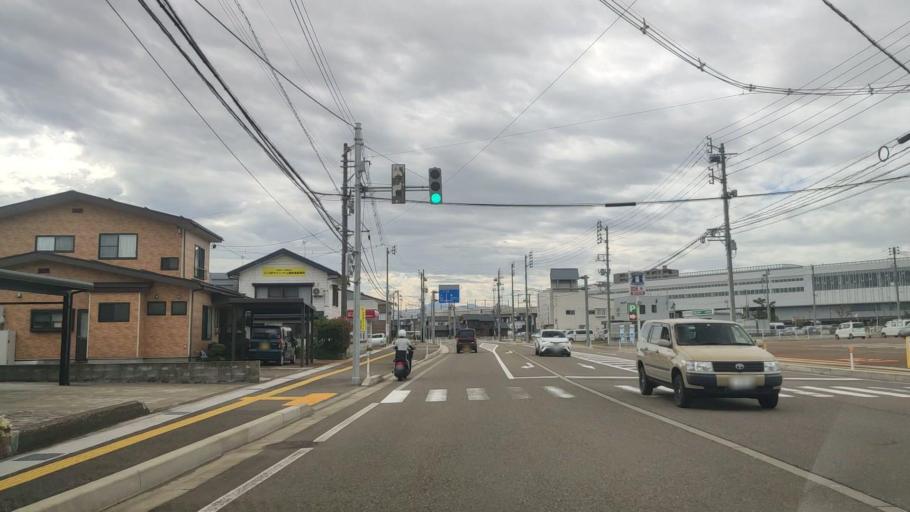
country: JP
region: Niigata
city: Joetsu
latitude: 37.0836
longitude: 138.2501
